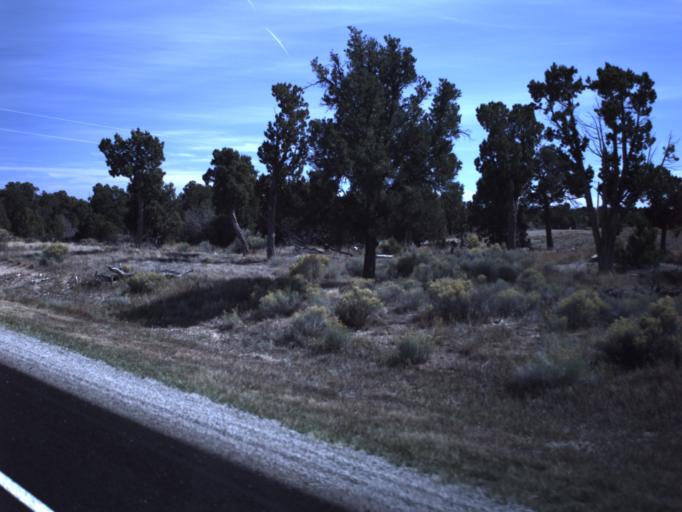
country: US
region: Colorado
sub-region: Dolores County
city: Dove Creek
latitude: 37.8227
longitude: -109.0640
